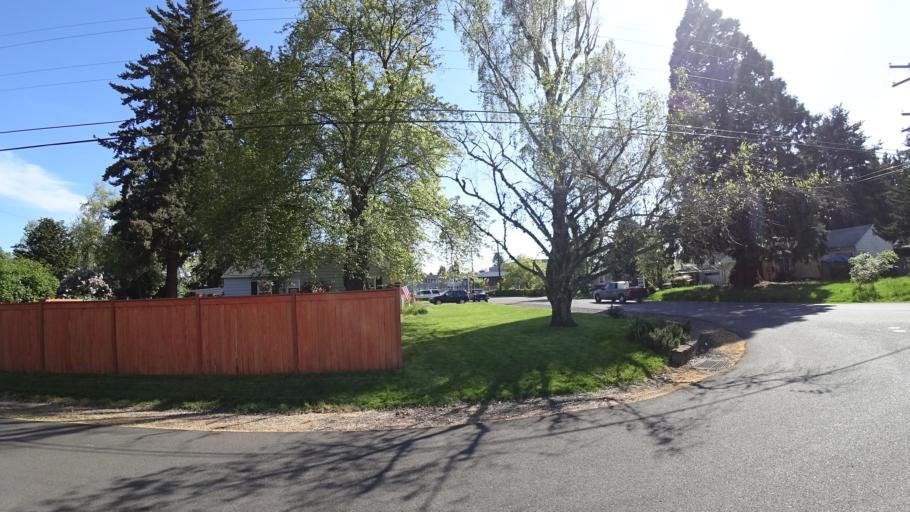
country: US
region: Oregon
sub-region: Washington County
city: Hillsboro
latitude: 45.5259
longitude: -122.9765
